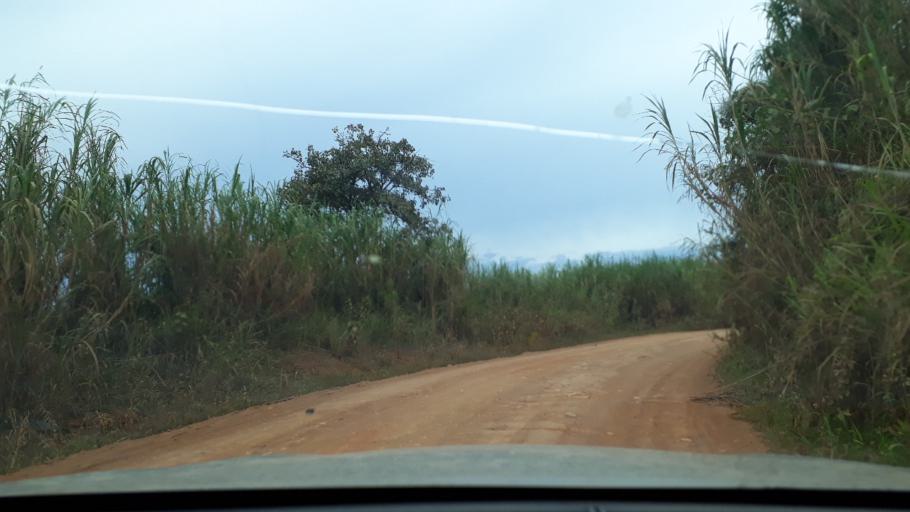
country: CD
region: Eastern Province
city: Bunia
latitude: 1.8086
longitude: 30.4139
